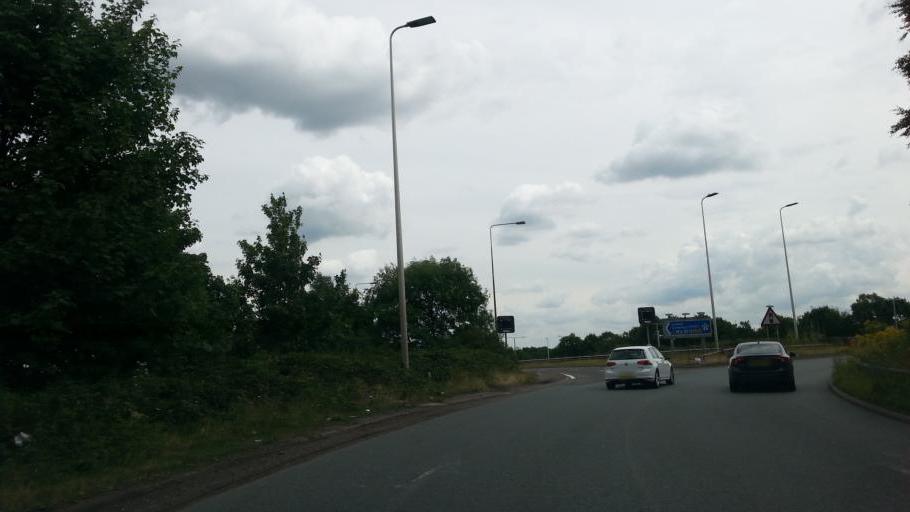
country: GB
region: England
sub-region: Solihull
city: Chelmsley Wood
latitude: 52.4776
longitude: -1.7065
